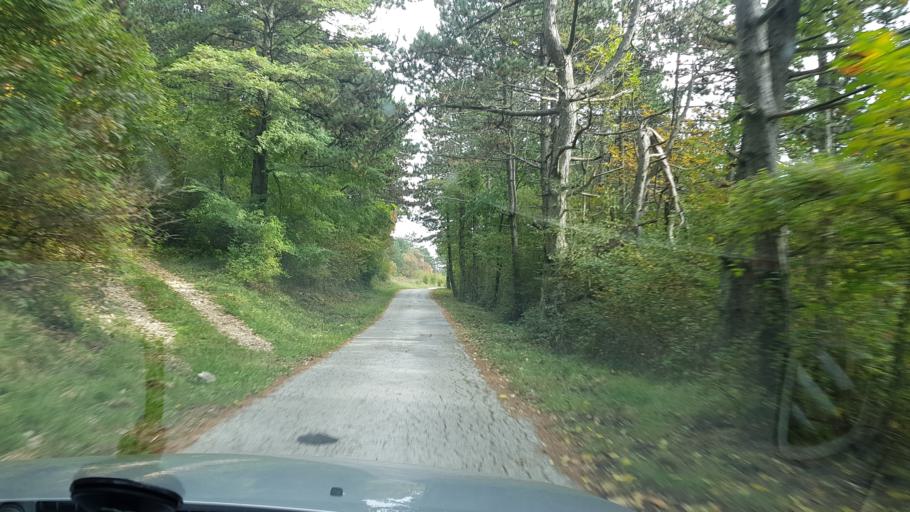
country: HR
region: Istarska
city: Buzet
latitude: 45.4497
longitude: 14.0209
